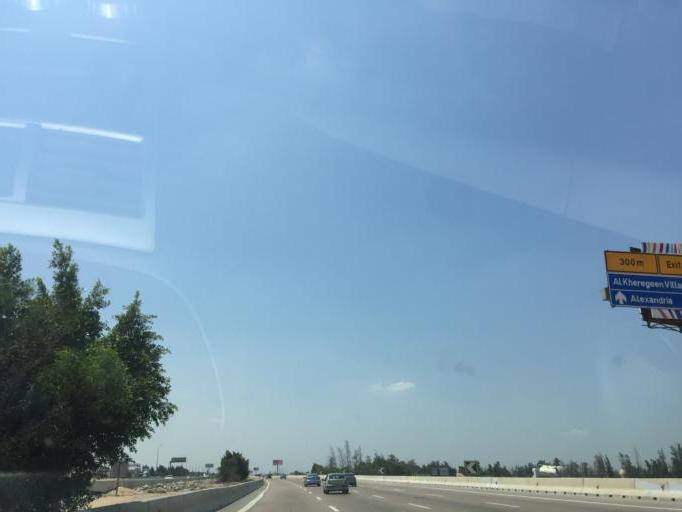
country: EG
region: Al Buhayrah
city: Beheira
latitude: 30.4423
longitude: 30.3272
